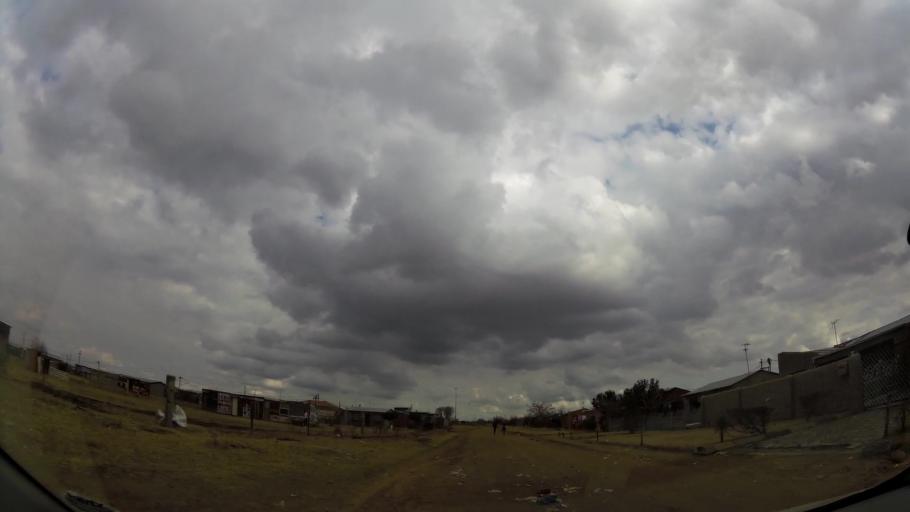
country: ZA
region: Orange Free State
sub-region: Fezile Dabi District Municipality
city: Sasolburg
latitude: -26.8610
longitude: 27.8655
